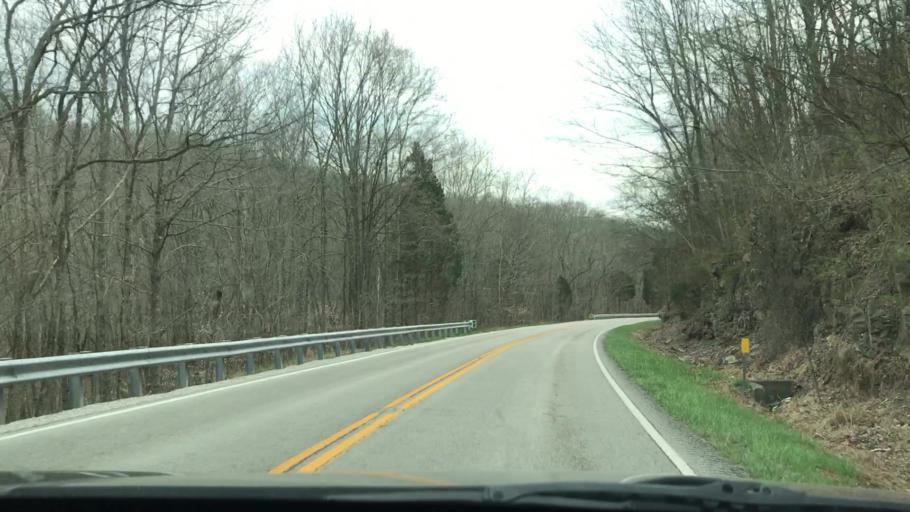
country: US
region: Kentucky
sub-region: Hart County
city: Munfordville
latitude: 37.3255
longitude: -85.7631
